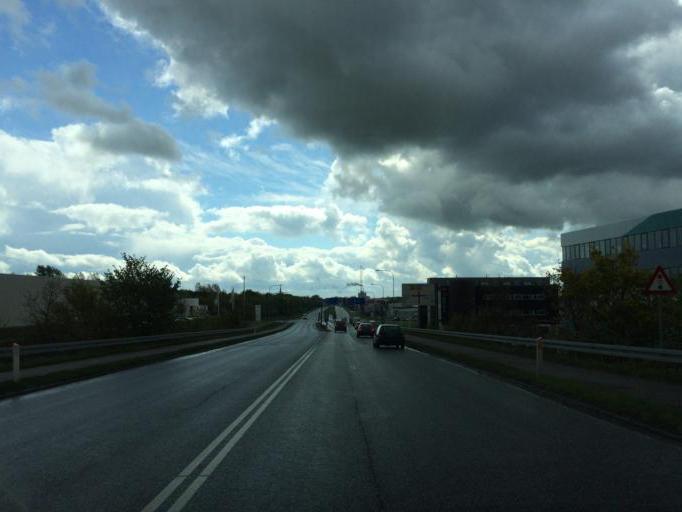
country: DK
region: Central Jutland
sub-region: Holstebro Kommune
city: Holstebro
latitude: 56.3738
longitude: 8.6238
